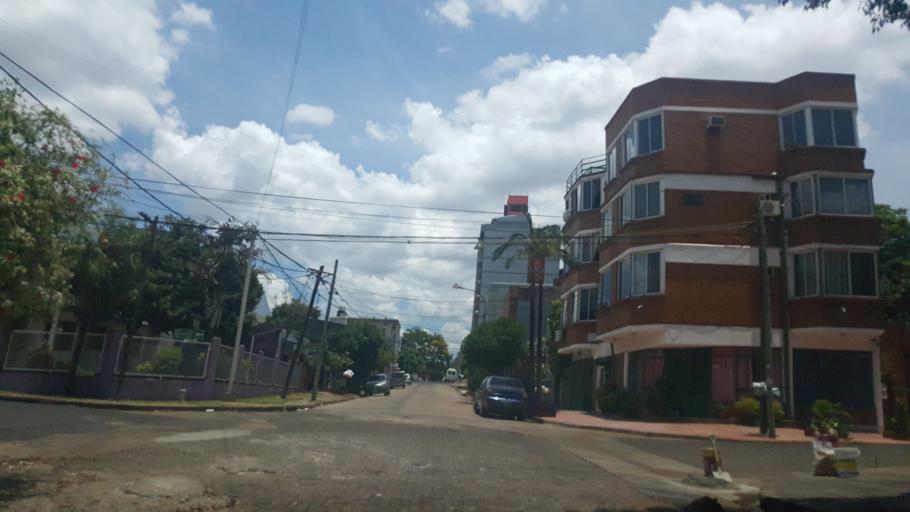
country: AR
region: Misiones
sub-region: Departamento de Capital
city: Posadas
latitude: -27.3648
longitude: -55.9038
